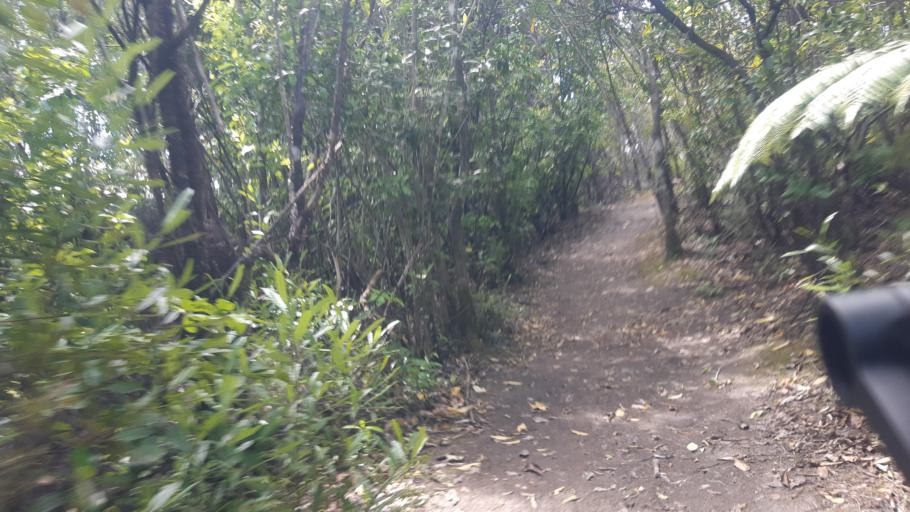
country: NZ
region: Marlborough
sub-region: Marlborough District
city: Picton
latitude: -41.2534
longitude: 174.0443
